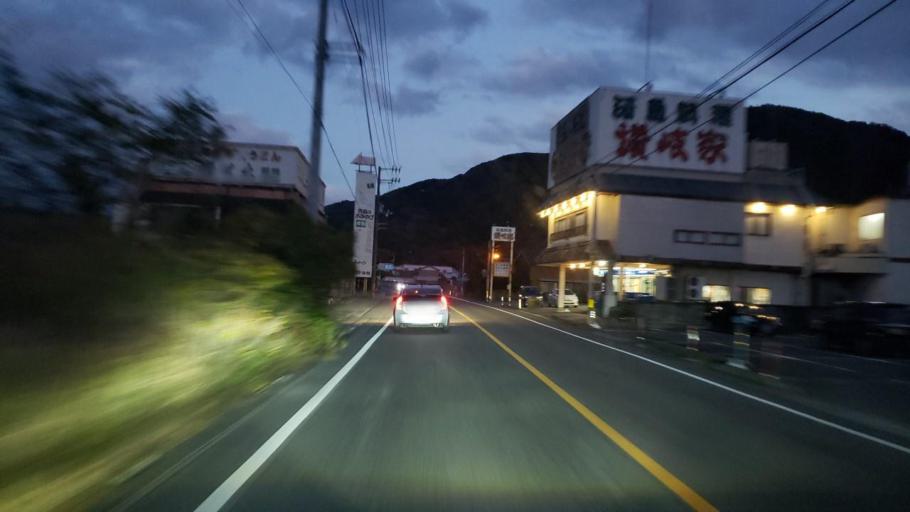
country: JP
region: Tokushima
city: Ishii
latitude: 34.2086
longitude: 134.4325
